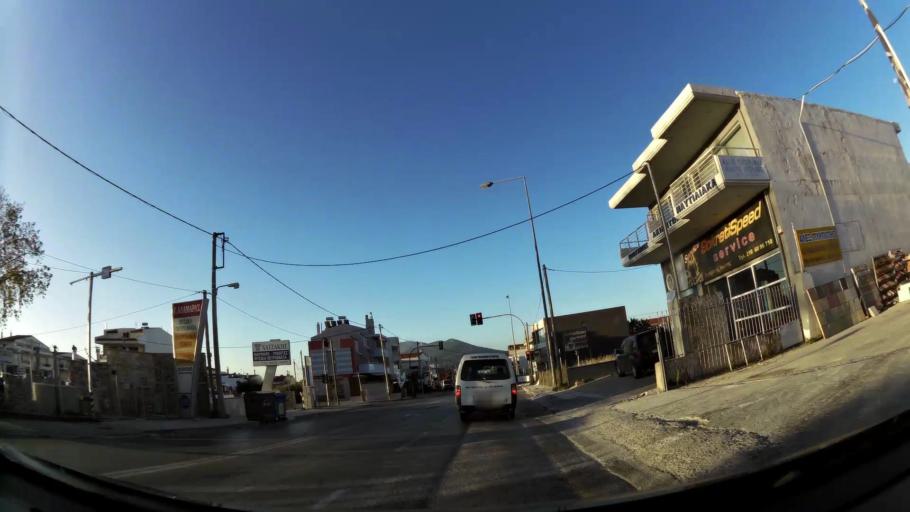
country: GR
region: Attica
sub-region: Nomarchia Anatolikis Attikis
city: Gerakas
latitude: 38.0322
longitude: 23.8565
